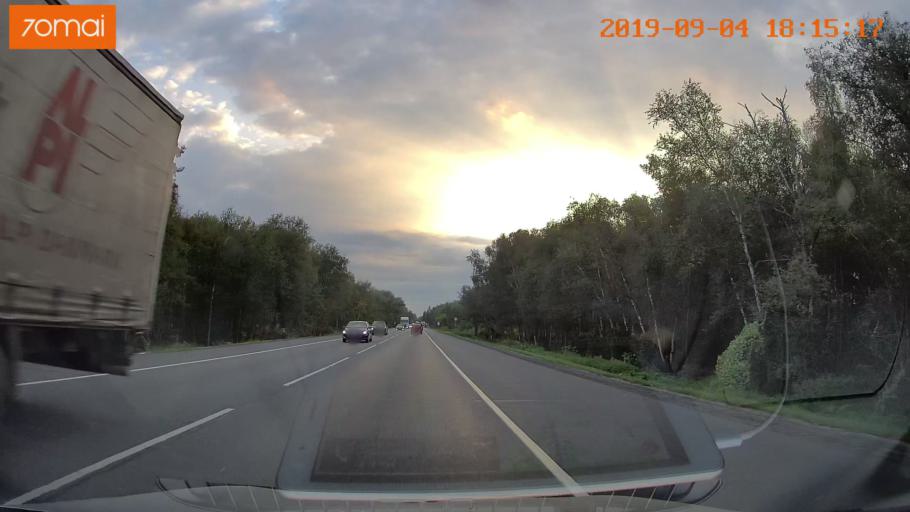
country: RU
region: Moskovskaya
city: Lopatinskiy
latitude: 55.3478
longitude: 38.7056
